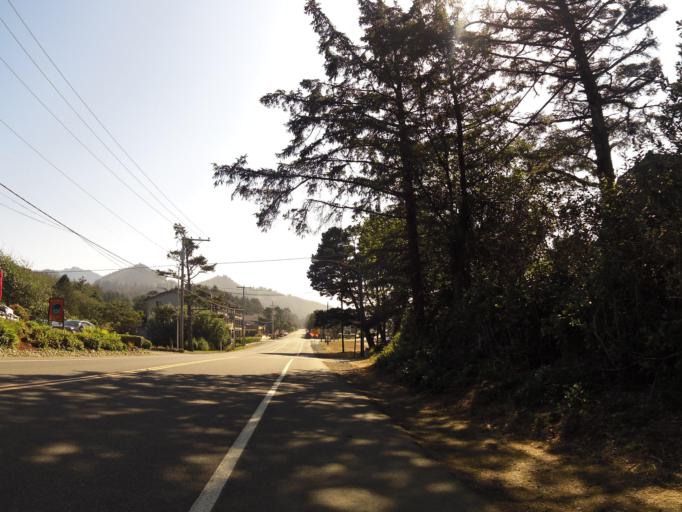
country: US
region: Oregon
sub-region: Clatsop County
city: Cannon Beach
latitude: 45.8736
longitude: -123.9599
